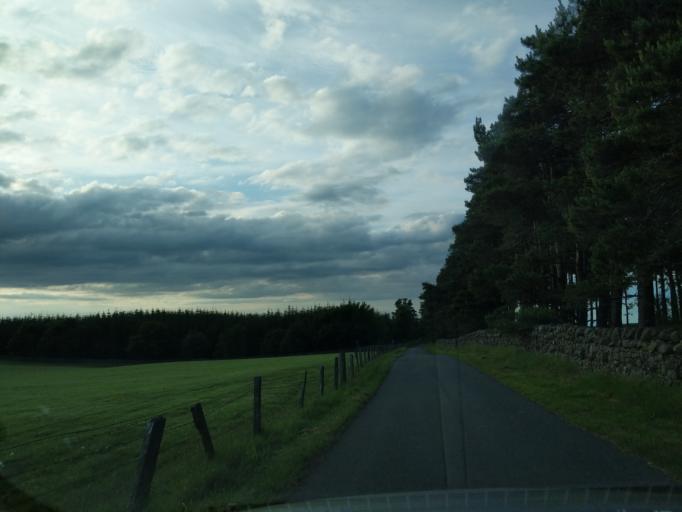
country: GB
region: Scotland
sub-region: Midlothian
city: Gorebridge
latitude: 55.7851
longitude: -3.0966
